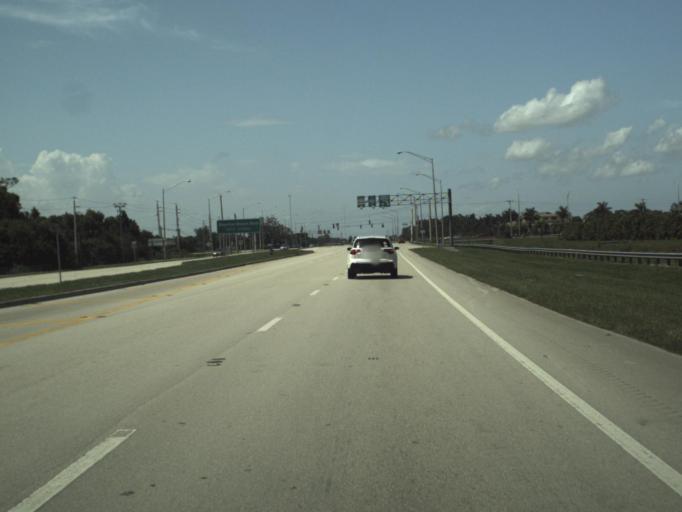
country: US
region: Florida
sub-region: Palm Beach County
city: Villages of Oriole
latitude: 26.5249
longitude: -80.2053
